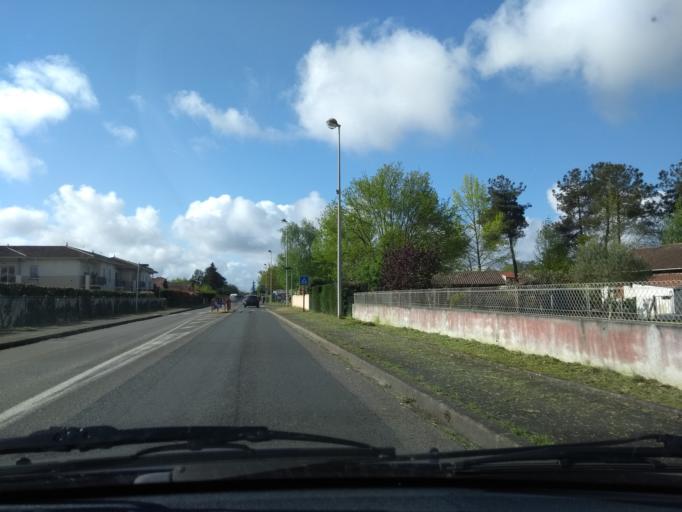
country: FR
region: Aquitaine
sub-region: Departement des Landes
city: Parentis-en-Born
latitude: 44.3563
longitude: -1.0738
